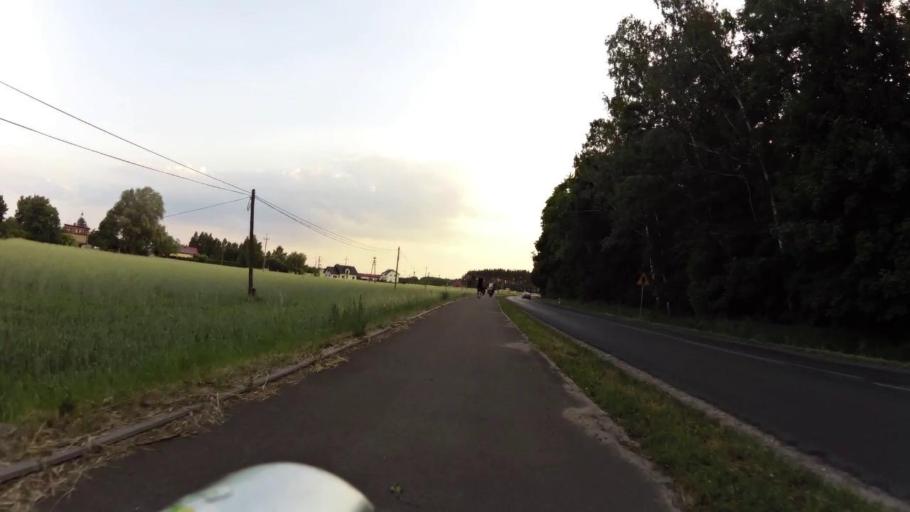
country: PL
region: Kujawsko-Pomorskie
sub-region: Powiat bydgoski
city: Dabrowa Chelminska
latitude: 53.1799
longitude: 18.3288
